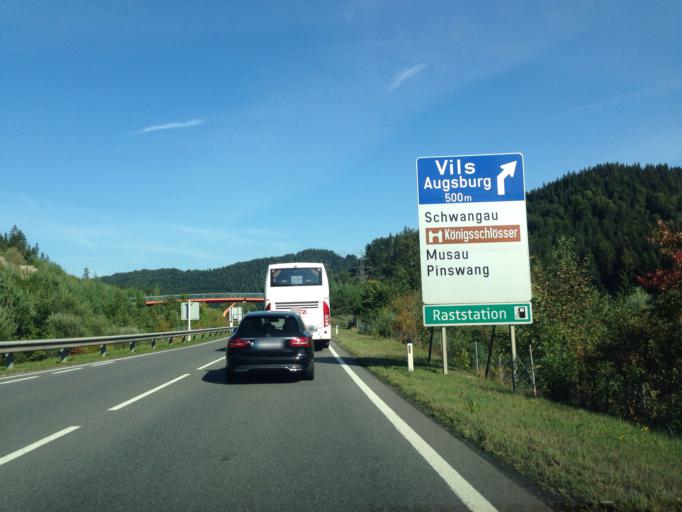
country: AT
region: Tyrol
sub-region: Politischer Bezirk Reutte
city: Musau
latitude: 47.5415
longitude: 10.6657
